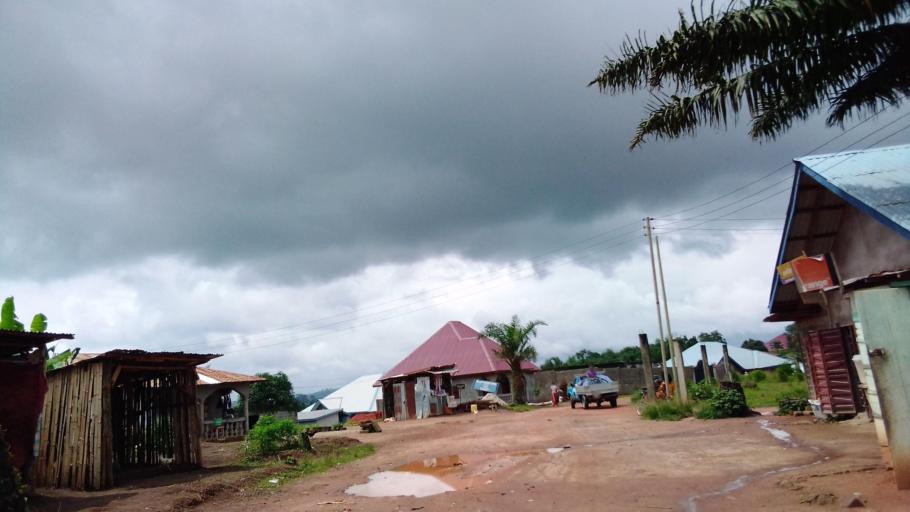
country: SL
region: Eastern Province
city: Kenema
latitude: 7.8671
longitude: -11.1729
